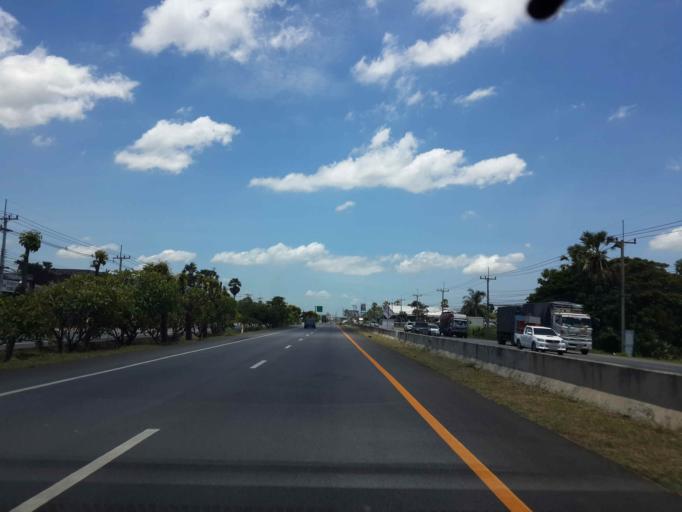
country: TH
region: Phetchaburi
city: Ban Lat
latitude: 13.0623
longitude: 99.9450
